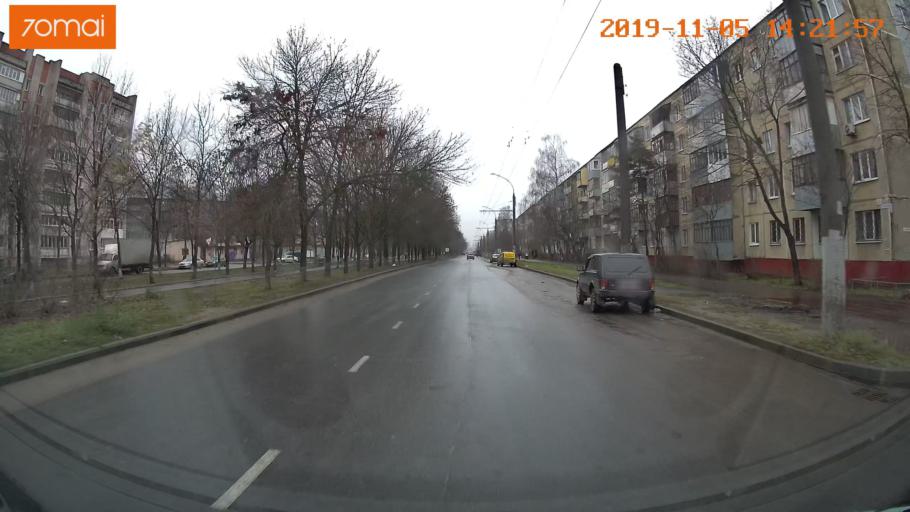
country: RU
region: Ivanovo
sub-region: Gorod Ivanovo
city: Ivanovo
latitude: 56.9610
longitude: 41.0082
